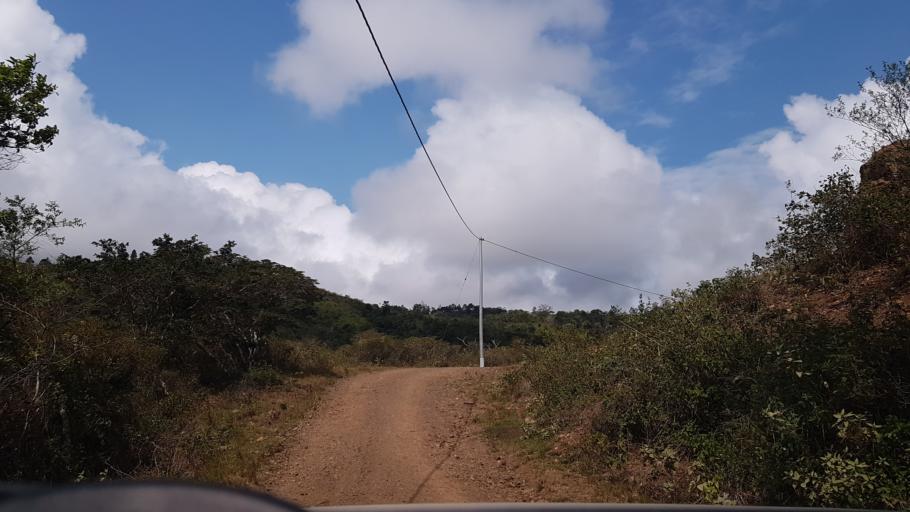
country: CO
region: Valle del Cauca
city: Yumbo
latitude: 3.6537
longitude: -76.5173
